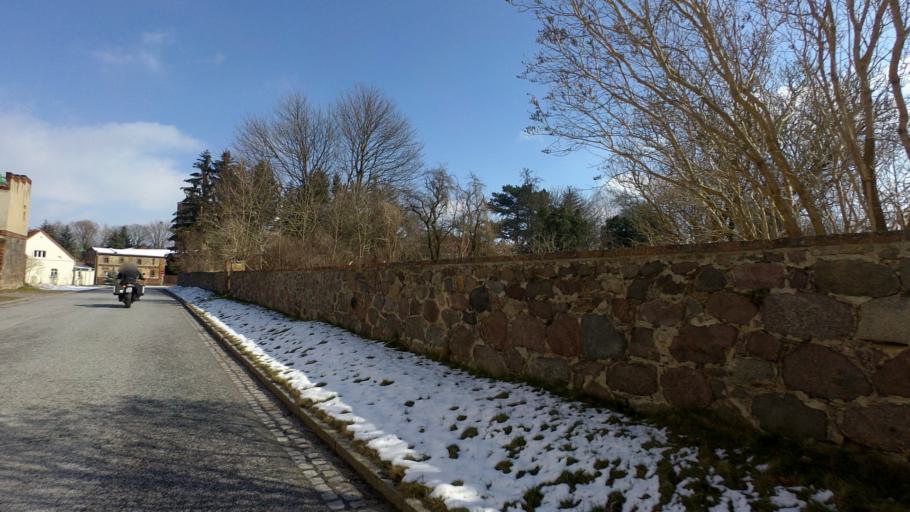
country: DE
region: Brandenburg
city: Werftpfuhl
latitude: 52.6926
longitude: 13.7811
